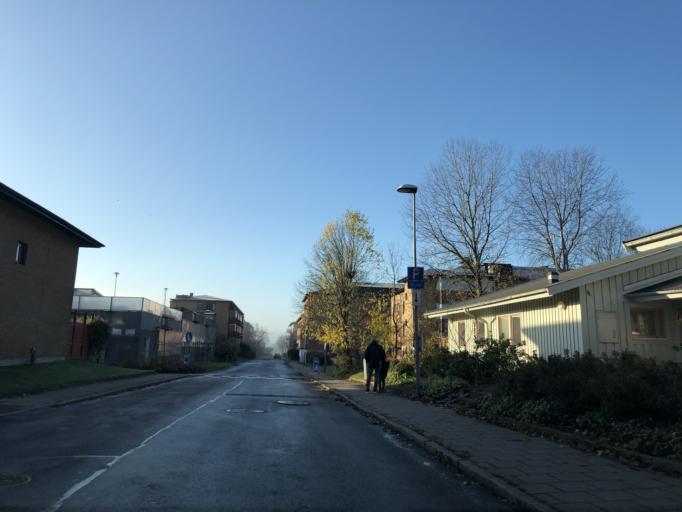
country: SE
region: Vaestra Goetaland
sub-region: Goteborg
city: Rannebergen
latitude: 57.7987
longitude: 12.0538
